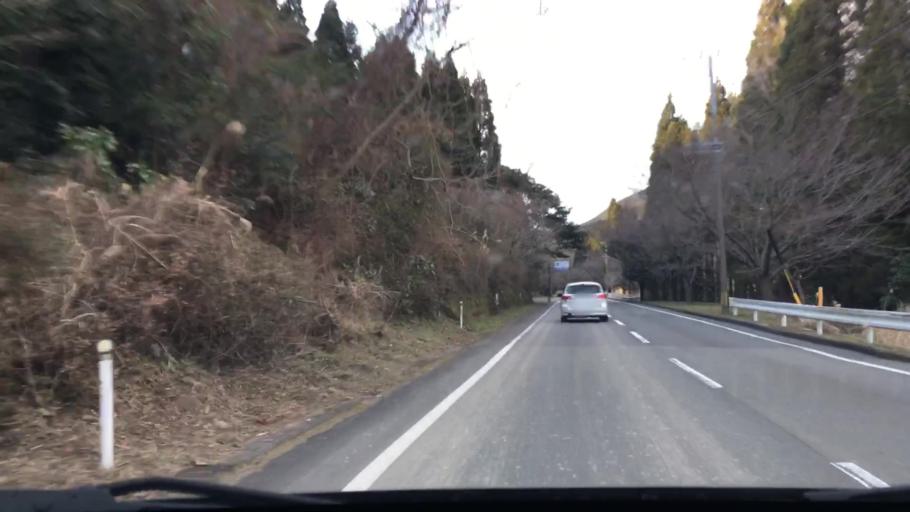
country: JP
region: Miyazaki
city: Miyazaki-shi
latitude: 31.7912
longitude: 131.3154
